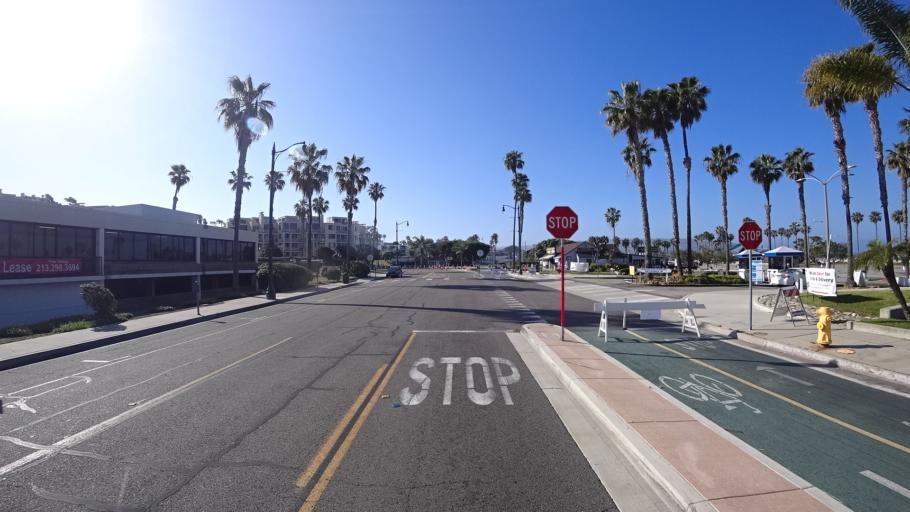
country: US
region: California
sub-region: Los Angeles County
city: Redondo Beach
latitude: 33.8442
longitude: -118.3924
